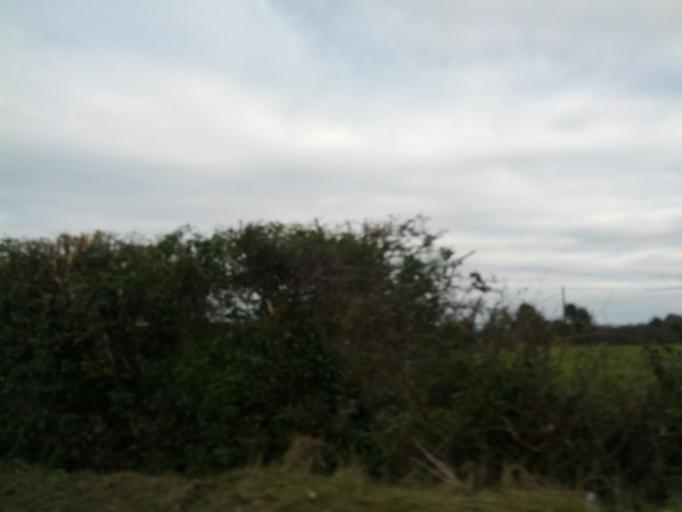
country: IE
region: Connaught
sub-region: County Galway
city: Gort
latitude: 53.1752
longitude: -8.8462
